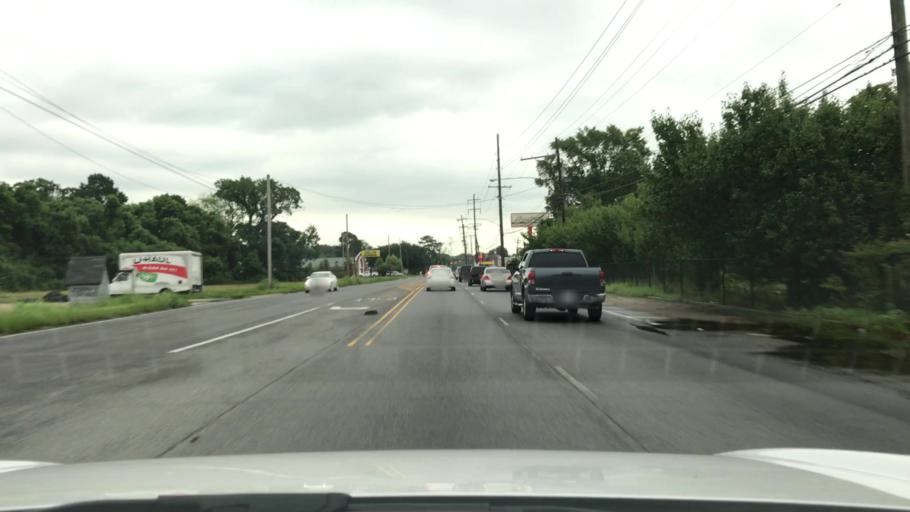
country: US
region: Louisiana
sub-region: East Baton Rouge Parish
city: Merrydale
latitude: 30.4725
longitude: -91.1214
